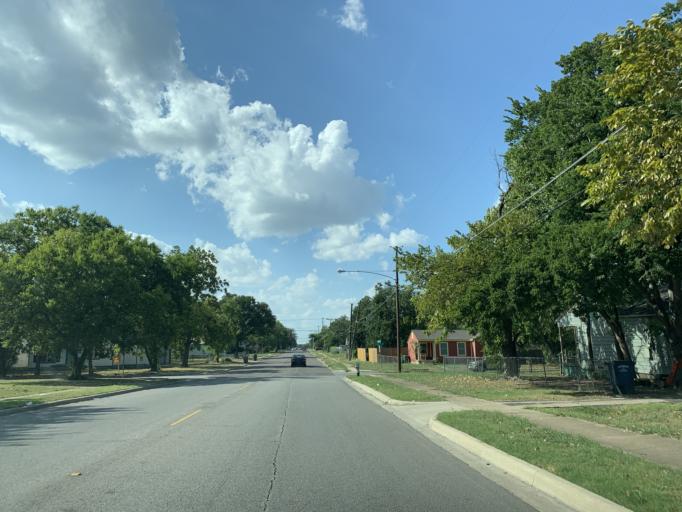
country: US
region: Texas
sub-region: Dallas County
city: Dallas
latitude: 32.7037
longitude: -96.7786
